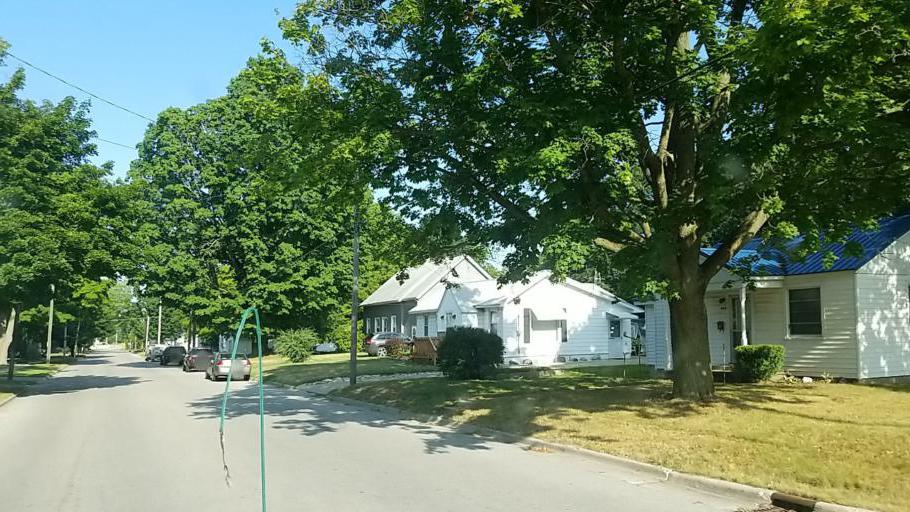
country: US
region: Michigan
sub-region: Newaygo County
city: Fremont
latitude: 43.4644
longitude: -85.9525
